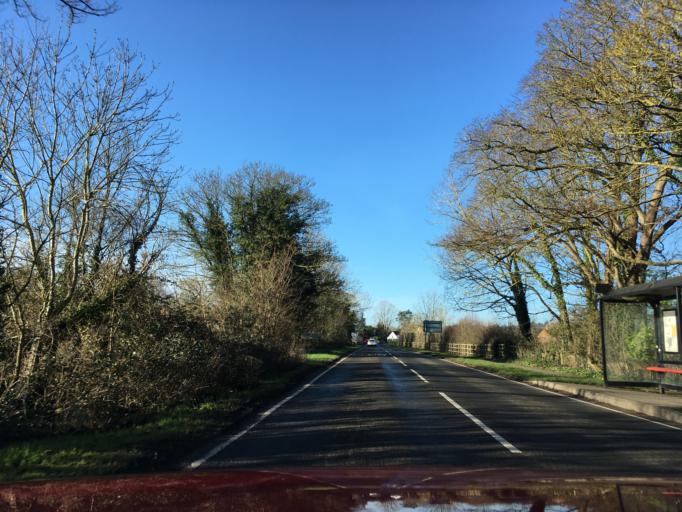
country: GB
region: England
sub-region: Warwickshire
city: Stratford-upon-Avon
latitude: 52.2032
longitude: -1.6639
